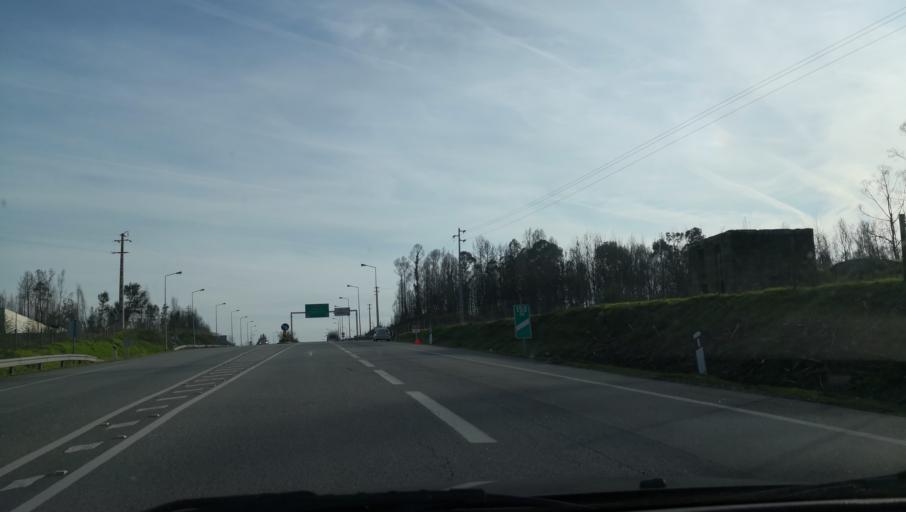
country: PT
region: Viseu
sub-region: Concelho de Tondela
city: Tondela
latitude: 40.5044
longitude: -8.0845
